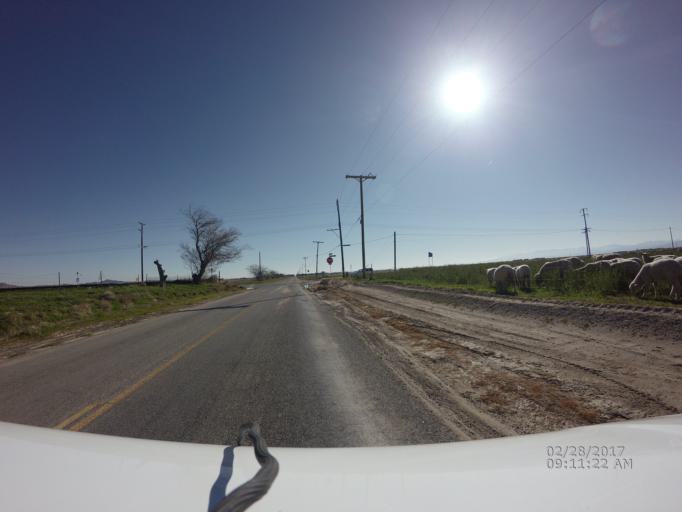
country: US
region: California
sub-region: Kern County
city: Rosamond
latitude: 34.8201
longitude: -118.2911
